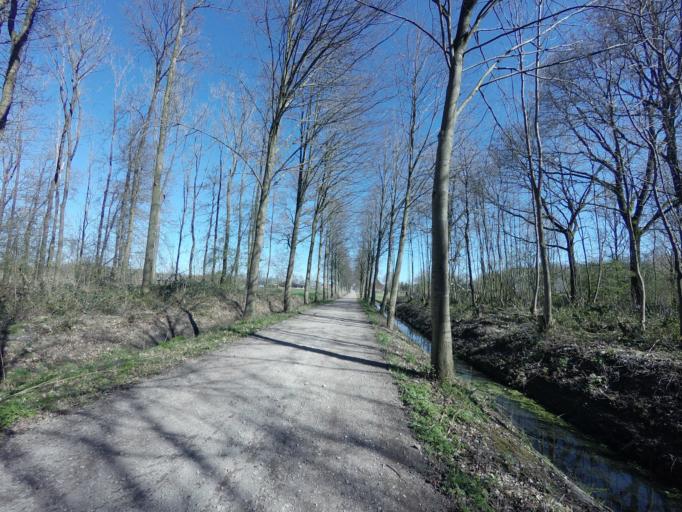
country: NL
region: Utrecht
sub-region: Gemeente Utrechtse Heuvelrug
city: Doorn
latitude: 52.0137
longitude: 5.3069
